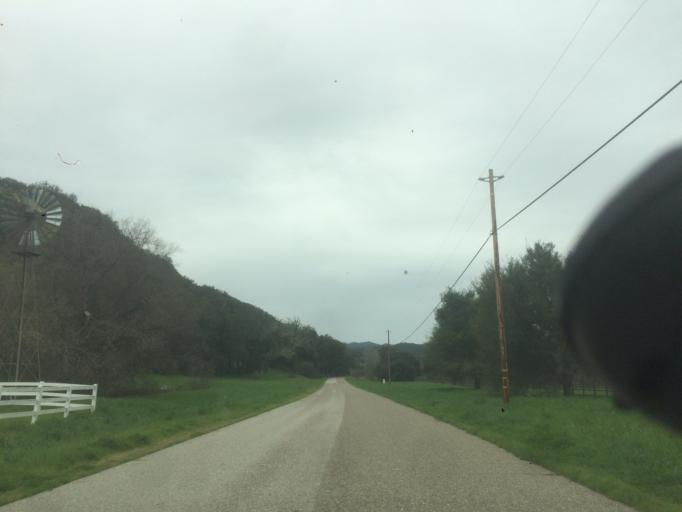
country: US
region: California
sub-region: San Luis Obispo County
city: Nipomo
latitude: 35.2070
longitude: -120.4068
